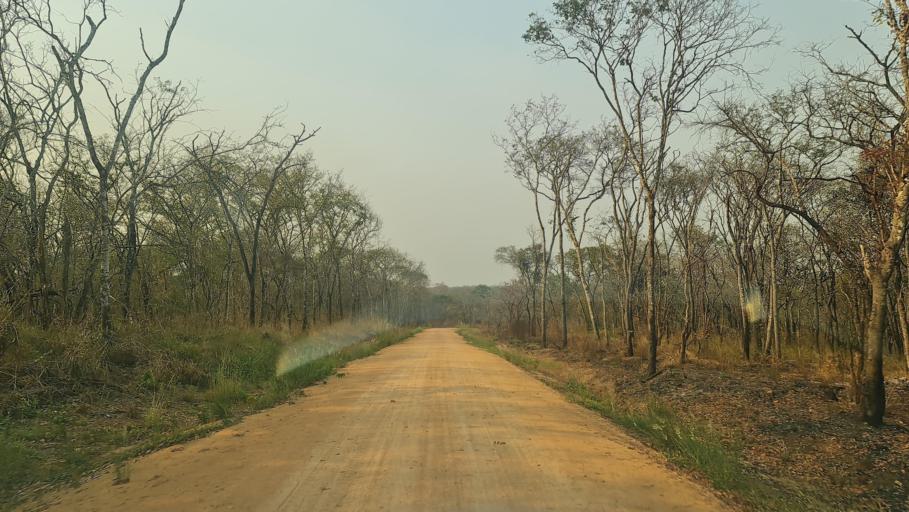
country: MZ
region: Zambezia
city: Quelimane
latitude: -17.1434
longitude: 37.1355
